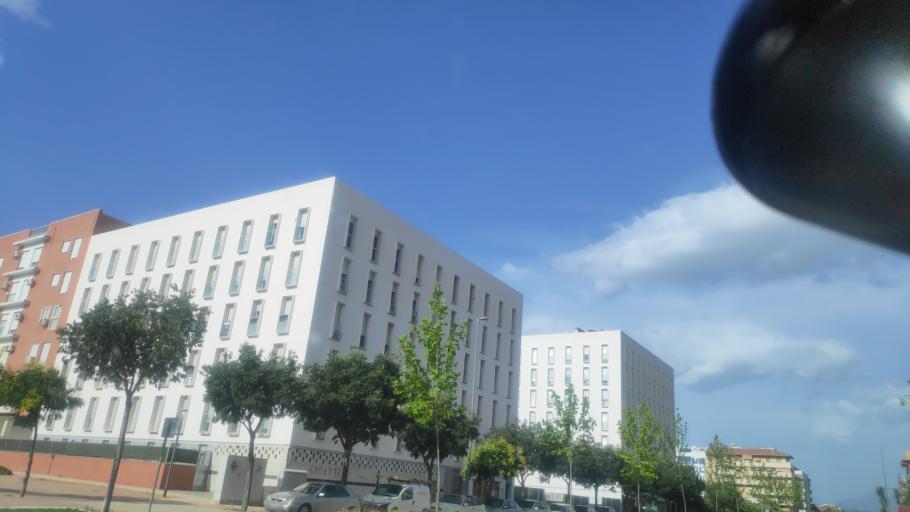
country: ES
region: Andalusia
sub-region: Provincia de Jaen
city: Jaen
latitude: 37.7878
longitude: -3.7930
